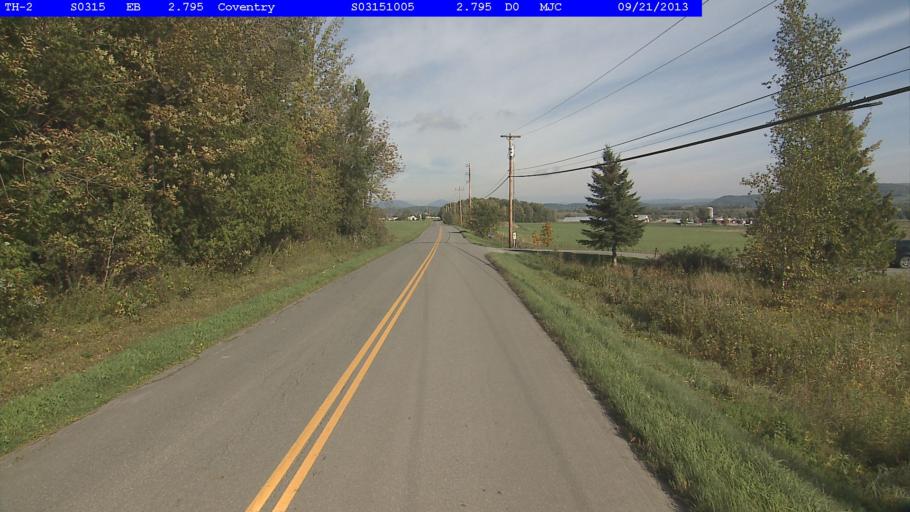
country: US
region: Vermont
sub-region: Orleans County
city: Newport
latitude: 44.8765
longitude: -72.2157
